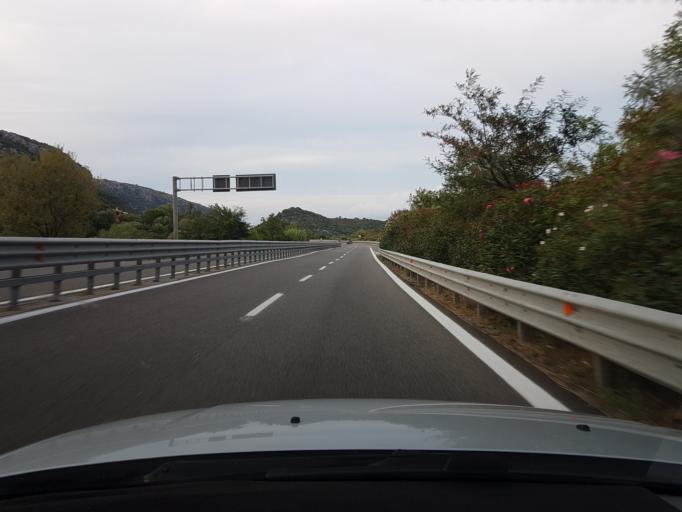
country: IT
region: Sardinia
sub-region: Provincia di Nuoro
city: Siniscola
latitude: 40.5873
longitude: 9.6919
